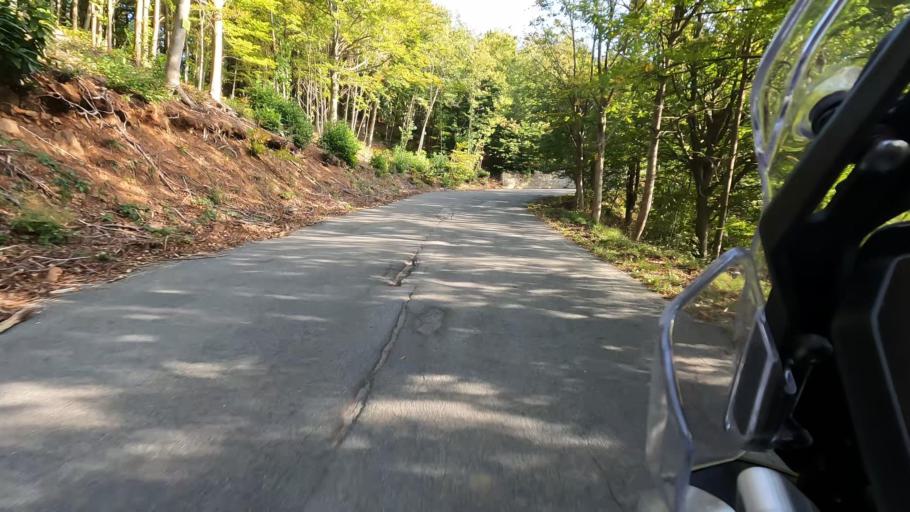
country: IT
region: Liguria
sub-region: Provincia di Savona
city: Urbe
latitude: 44.4733
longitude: 8.5607
